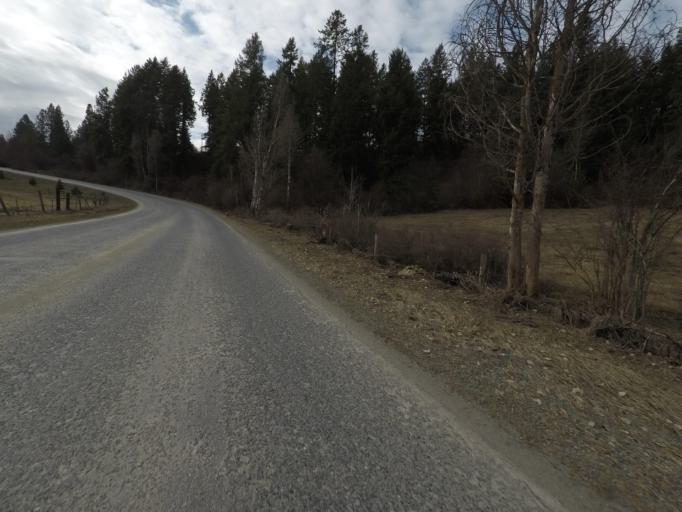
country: US
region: Washington
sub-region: Stevens County
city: Colville
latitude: 48.5123
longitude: -117.8684
